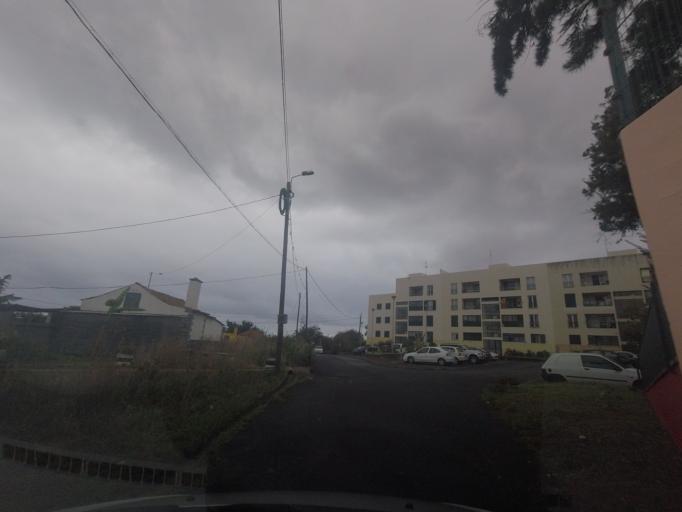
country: PT
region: Madeira
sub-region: Funchal
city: Funchal
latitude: 32.6433
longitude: -16.9333
